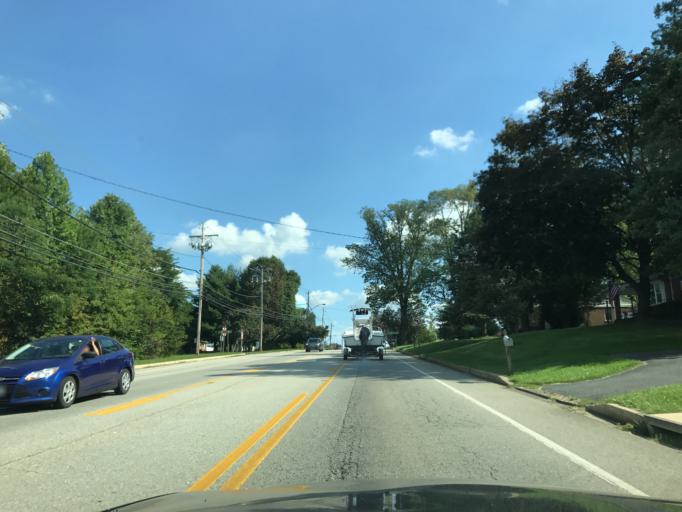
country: US
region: Maryland
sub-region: Harford County
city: South Bel Air
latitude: 39.5413
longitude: -76.3081
